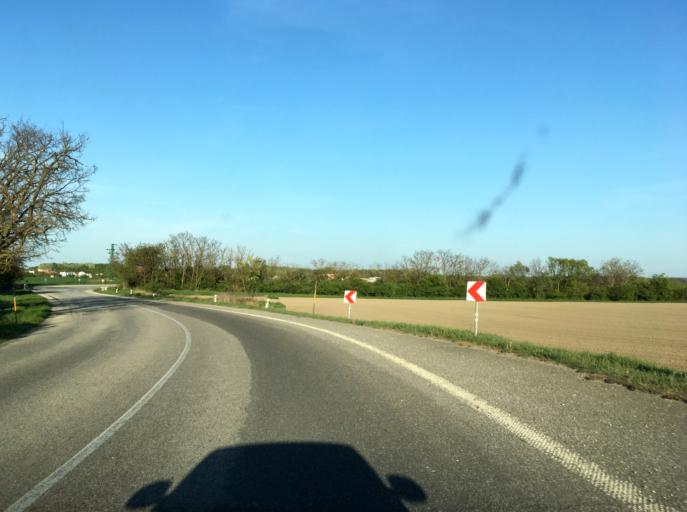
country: HU
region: Gyor-Moson-Sopron
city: Rajka
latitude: 48.0243
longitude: 17.1844
